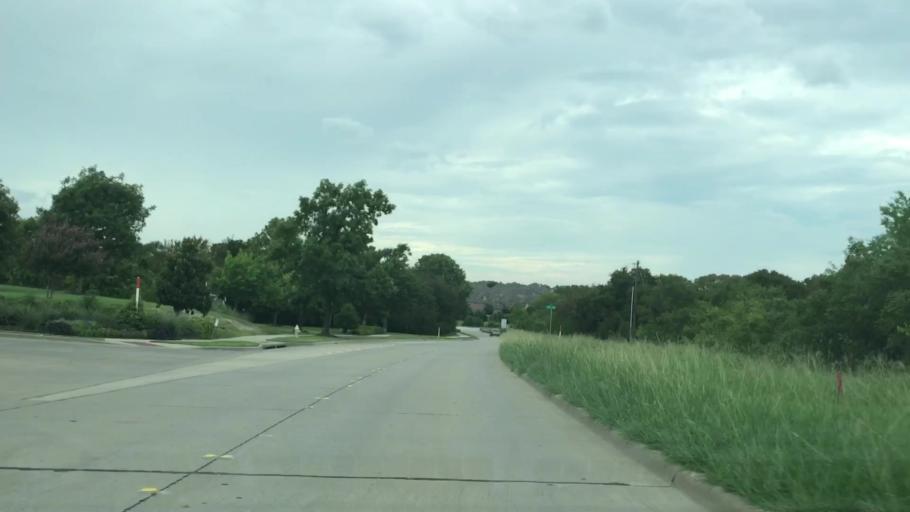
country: US
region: Texas
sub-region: Collin County
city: Prosper
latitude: 33.1883
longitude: -96.7867
